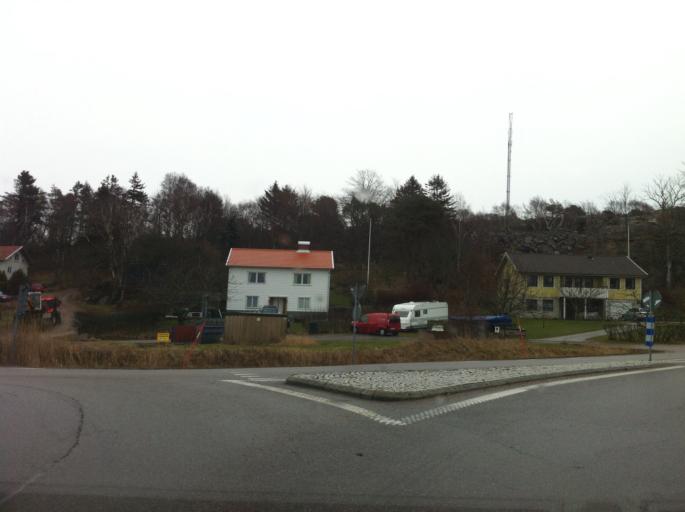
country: SE
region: Vaestra Goetaland
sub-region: Sotenas Kommun
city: Kungshamn
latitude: 58.3938
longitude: 11.2636
